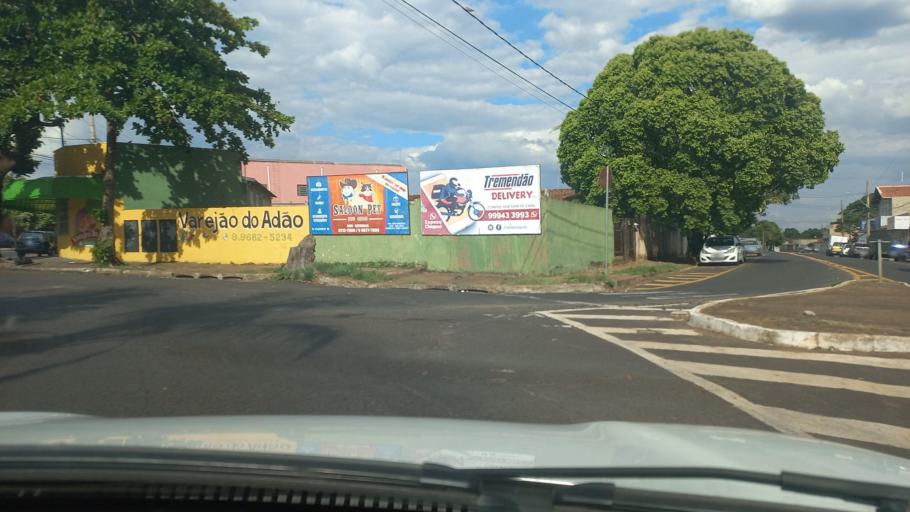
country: BR
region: Minas Gerais
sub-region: Uberaba
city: Uberaba
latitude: -19.7352
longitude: -47.9175
